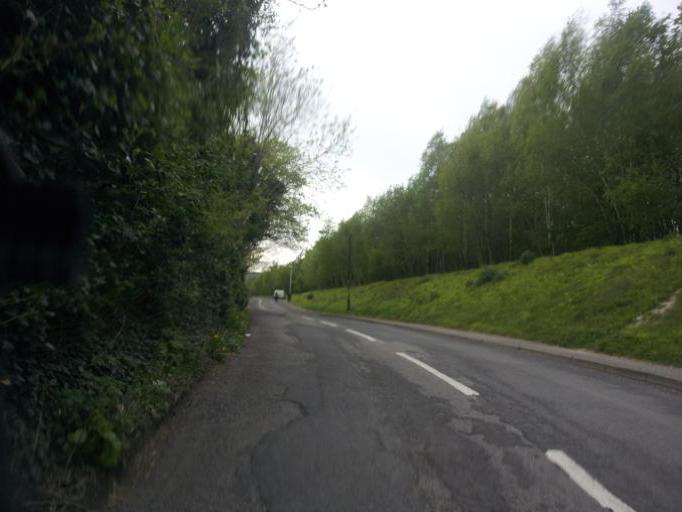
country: GB
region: England
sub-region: Medway
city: Halling
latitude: 51.3532
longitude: 0.4343
